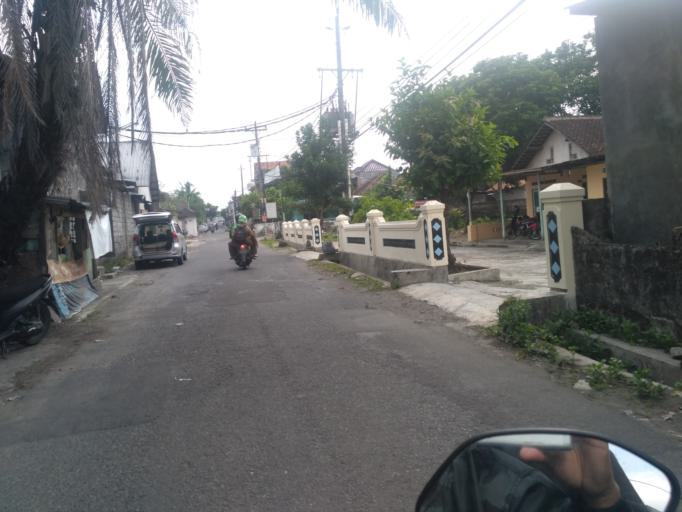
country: ID
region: Daerah Istimewa Yogyakarta
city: Melati
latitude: -7.7535
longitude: 110.3633
